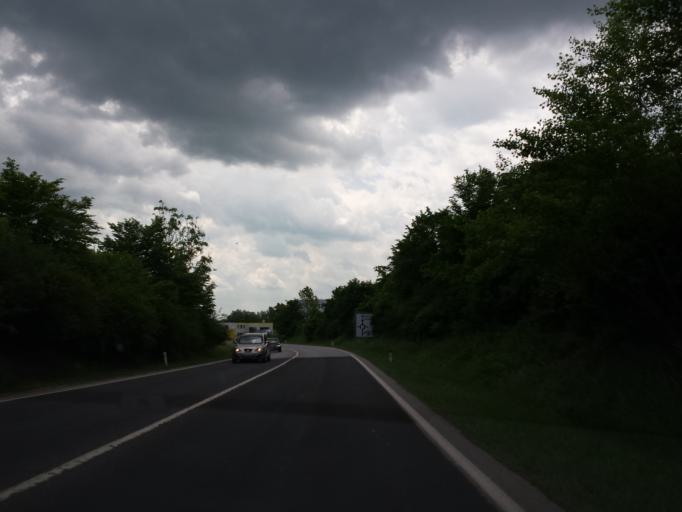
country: AT
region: Lower Austria
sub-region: Politischer Bezirk Wien-Umgebung
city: Fischamend Dorf
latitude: 48.1232
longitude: 16.5973
